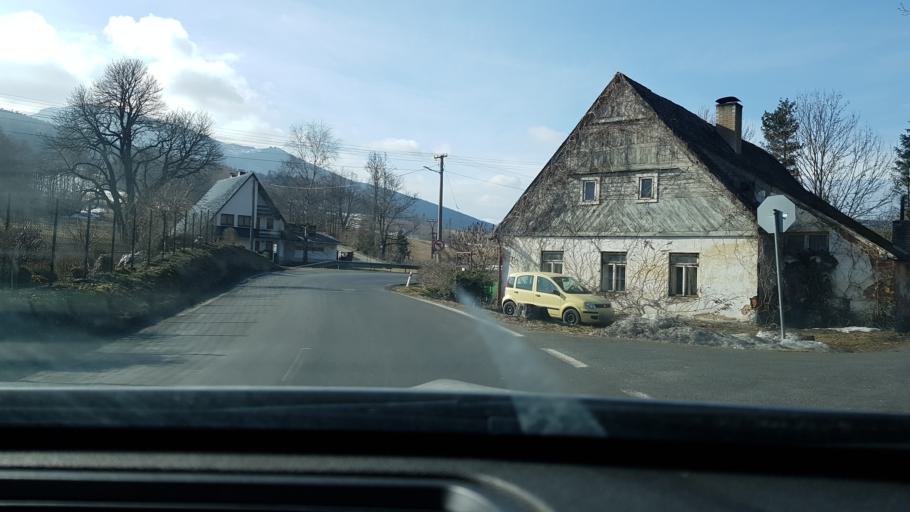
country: CZ
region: Olomoucky
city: Vapenna
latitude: 50.2266
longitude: 17.1205
